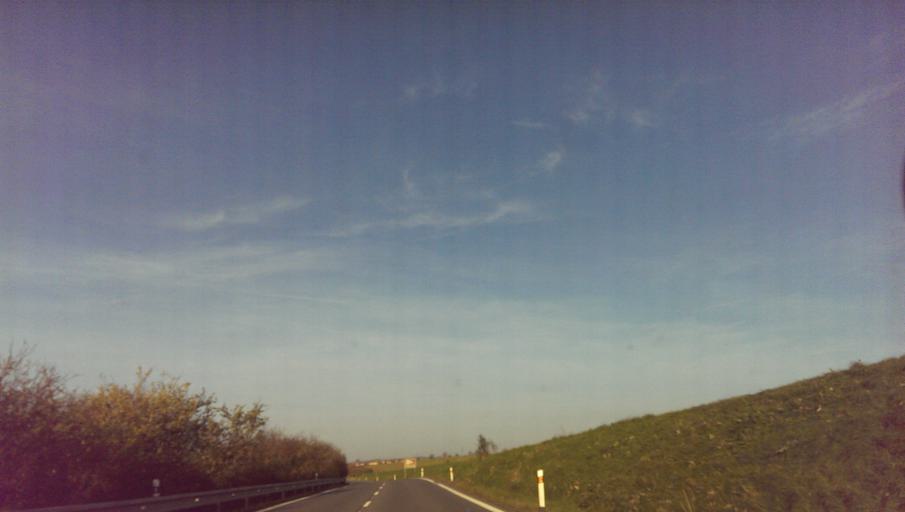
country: CZ
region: Zlin
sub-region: Okres Zlin
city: Ostrozska Nova Ves
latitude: 49.0241
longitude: 17.4532
